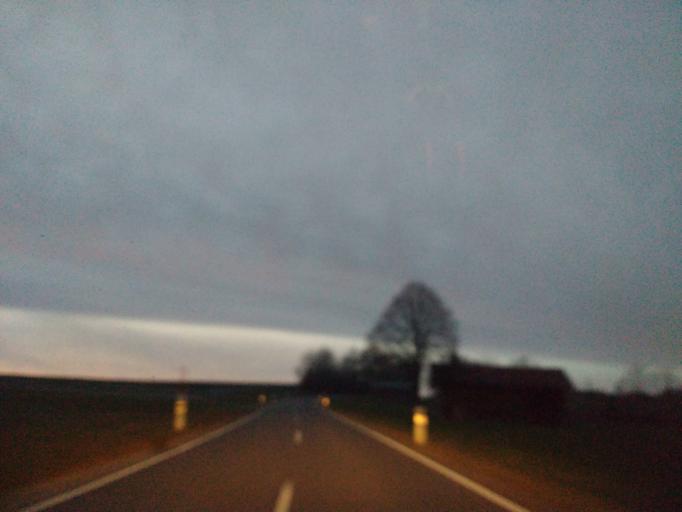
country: DE
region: Bavaria
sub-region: Swabia
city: Bidingen
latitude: 47.8381
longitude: 10.7211
